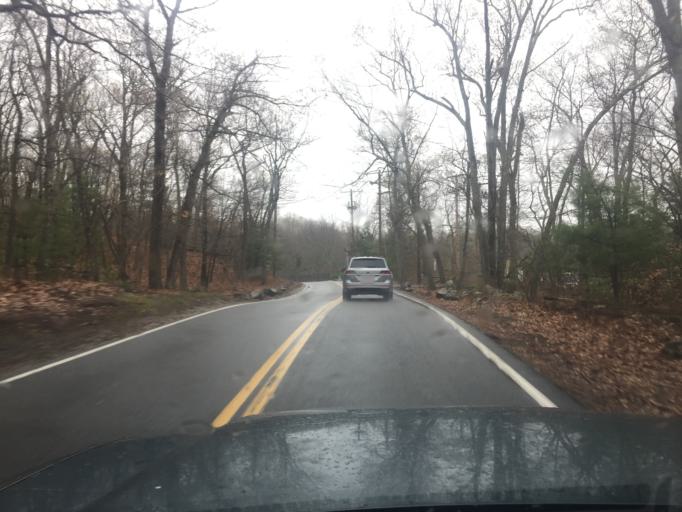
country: US
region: Massachusetts
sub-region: Norfolk County
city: Westwood
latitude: 42.2288
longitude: -71.2486
